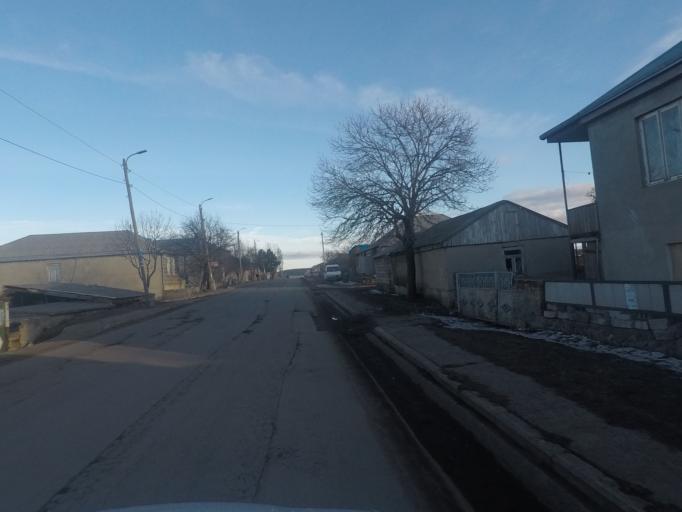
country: GE
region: Kvemo Kartli
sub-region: Tsalka
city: Tsalka
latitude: 41.6031
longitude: 44.0498
